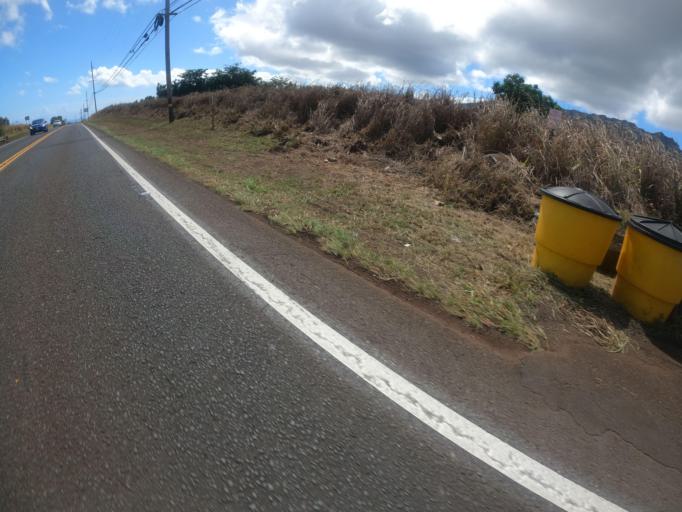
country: US
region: Hawaii
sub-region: Honolulu County
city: Village Park
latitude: 21.4324
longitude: -158.0572
